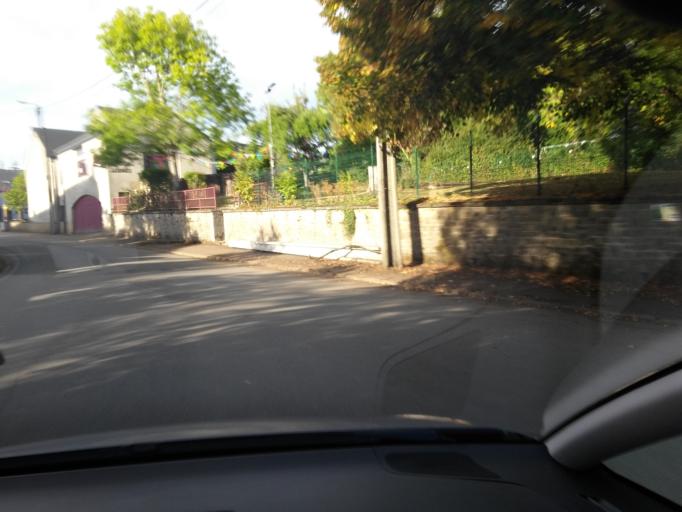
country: BE
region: Wallonia
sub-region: Province du Luxembourg
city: Attert
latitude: 49.7560
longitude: 5.7264
